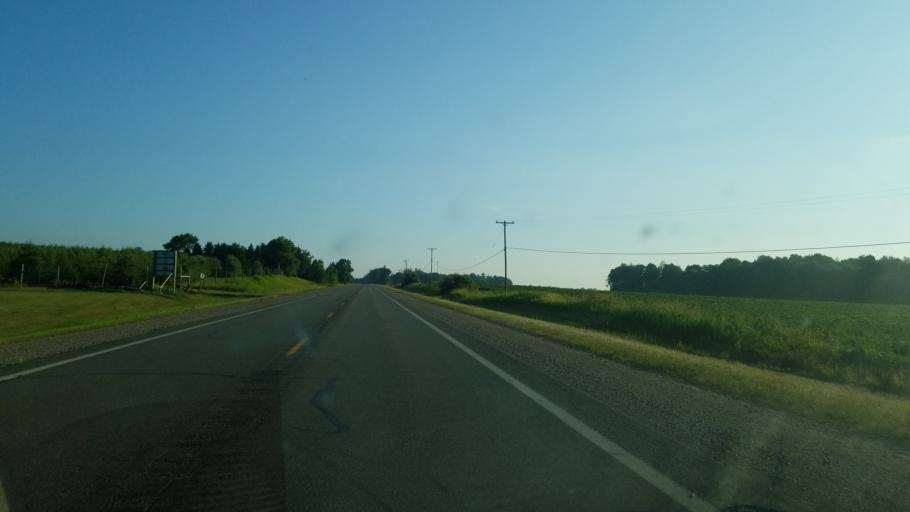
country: US
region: Michigan
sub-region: Montcalm County
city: Stanton
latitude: 43.3390
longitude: -85.0884
